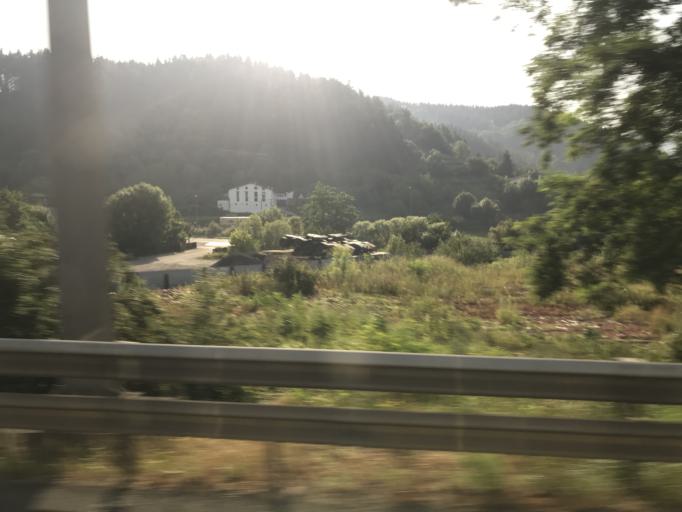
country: ES
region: Basque Country
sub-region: Provincia de Guipuzcoa
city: Villafranca de Ordizia
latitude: 43.0570
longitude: -2.1709
